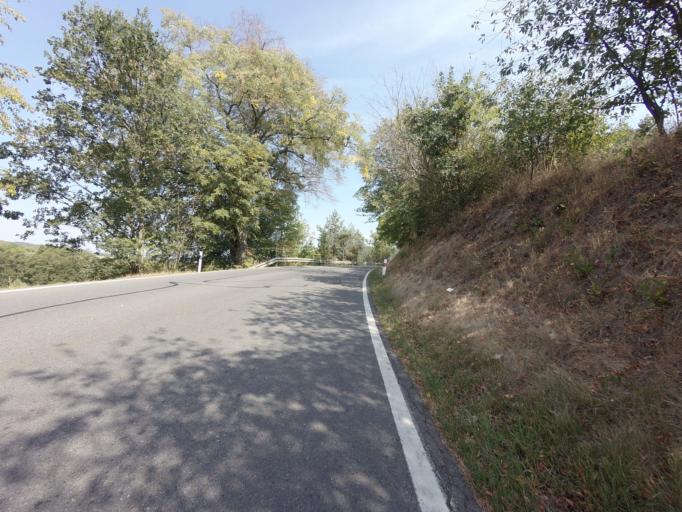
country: CZ
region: Central Bohemia
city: Petrovice
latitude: 49.5764
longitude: 14.3759
